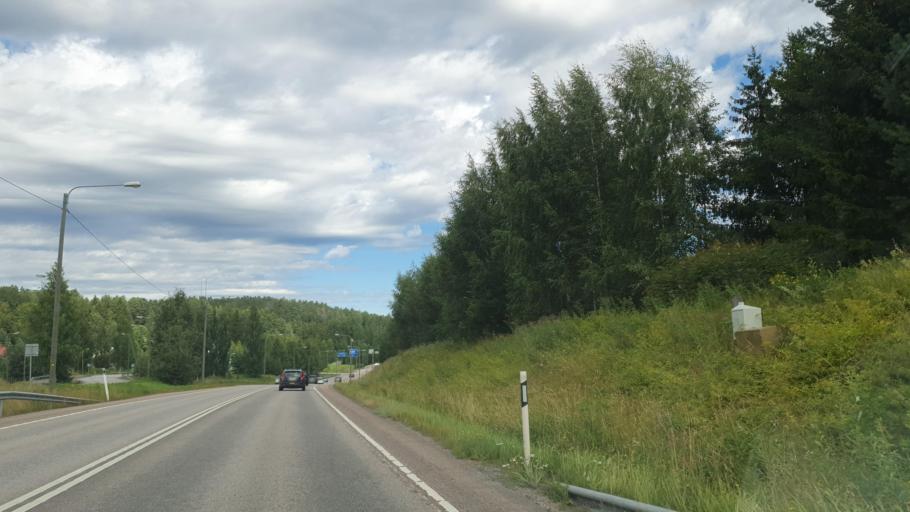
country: FI
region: Central Finland
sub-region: Jyvaeskylae
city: Korpilahti
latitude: 62.0145
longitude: 25.5467
